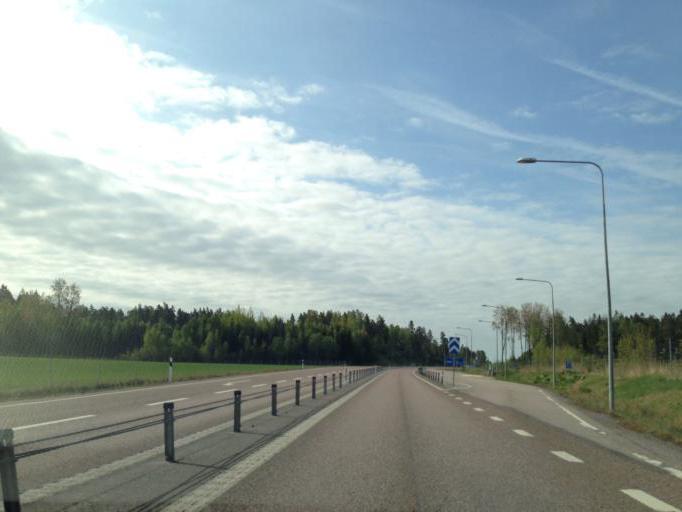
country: SE
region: Soedermanland
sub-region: Flens Kommun
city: Malmkoping
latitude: 59.1440
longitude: 16.7119
